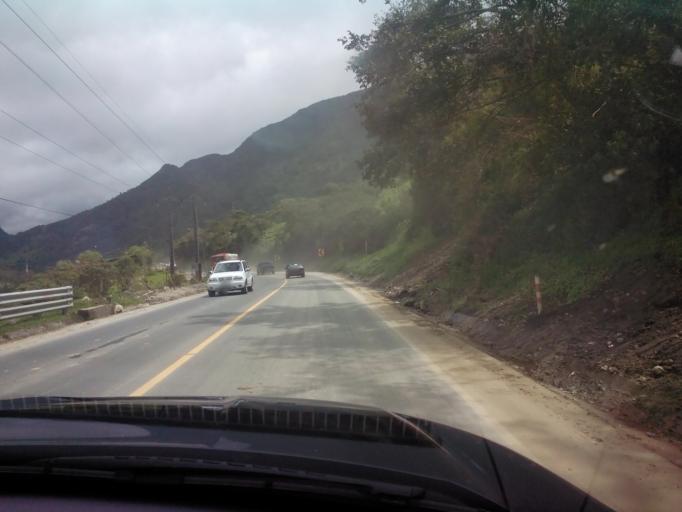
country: EC
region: Pichincha
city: Sangolqui
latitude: -0.3697
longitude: -78.1038
